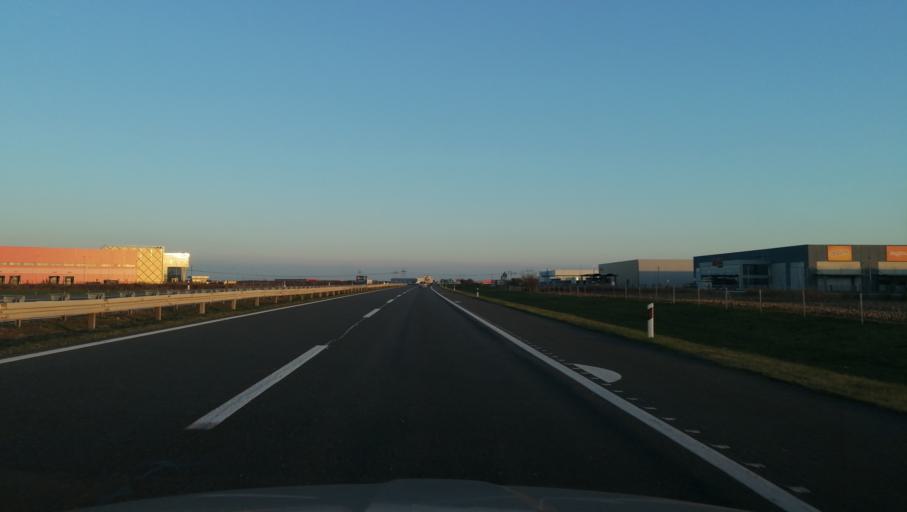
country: RS
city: Simanovci
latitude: 44.8893
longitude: 20.0924
